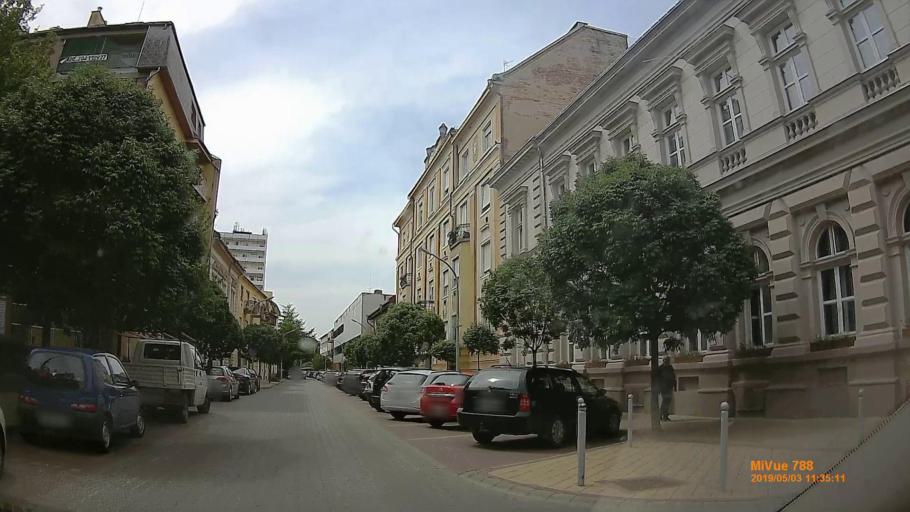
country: HU
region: Jasz-Nagykun-Szolnok
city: Szolnok
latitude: 47.1746
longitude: 20.1965
